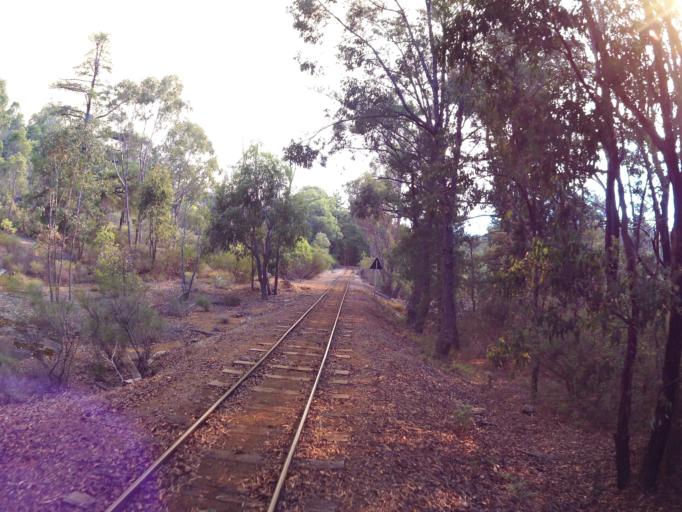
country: AU
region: Western Australia
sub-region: Waroona
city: Waroona
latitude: -32.7368
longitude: 116.1338
